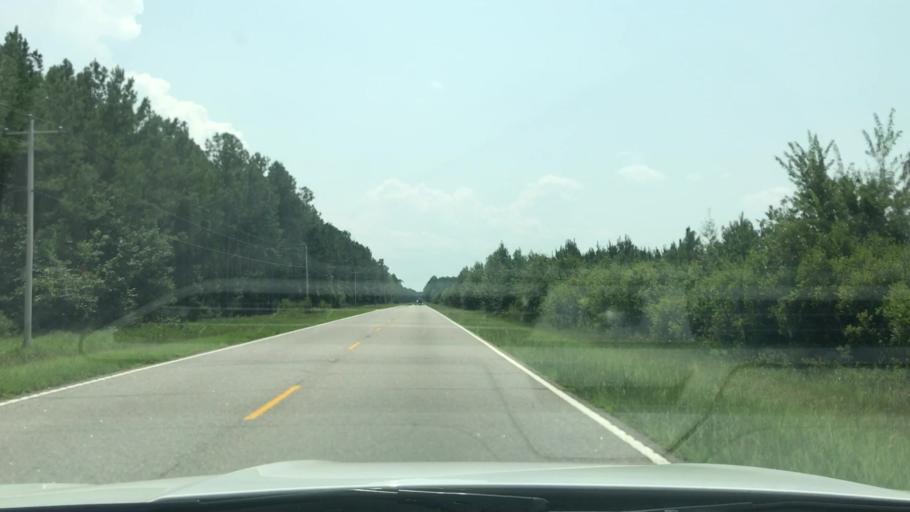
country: US
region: South Carolina
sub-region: Georgetown County
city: Georgetown
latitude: 33.5146
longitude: -79.2496
